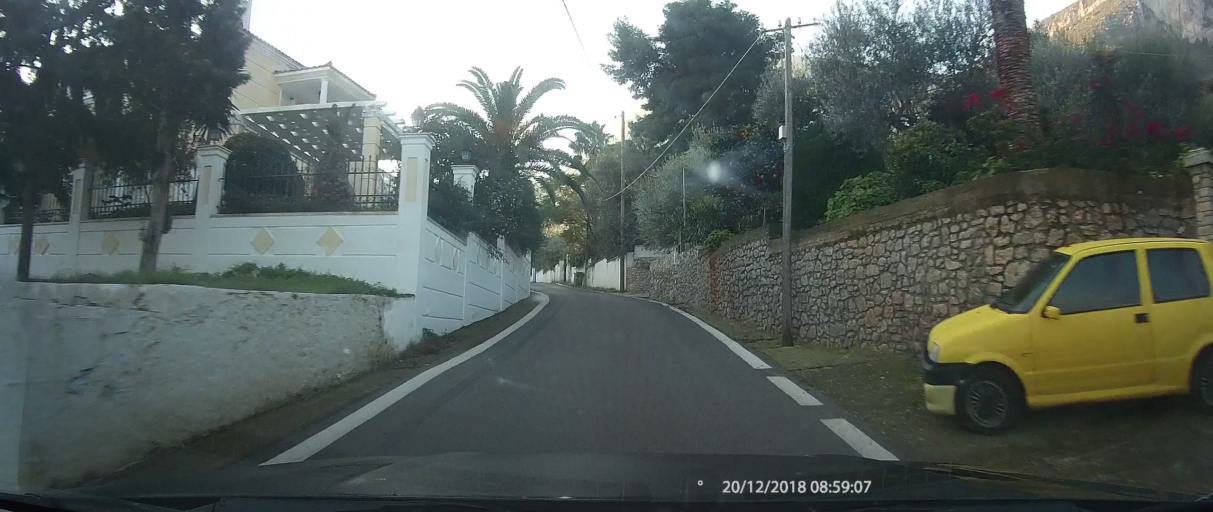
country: GR
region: Peloponnese
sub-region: Nomos Lakonias
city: Sykea
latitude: 36.9655
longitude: 22.9876
